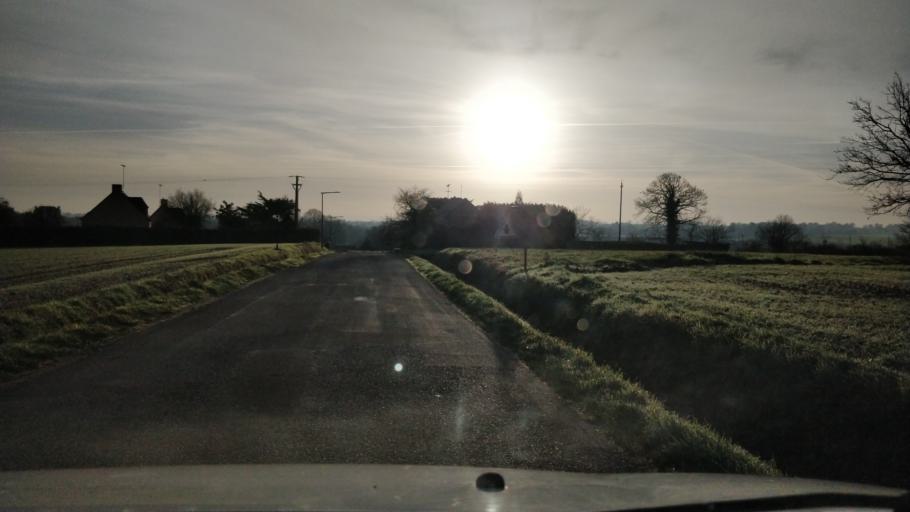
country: FR
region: Brittany
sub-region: Departement d'Ille-et-Vilaine
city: Bais
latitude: 48.0092
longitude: -1.2976
